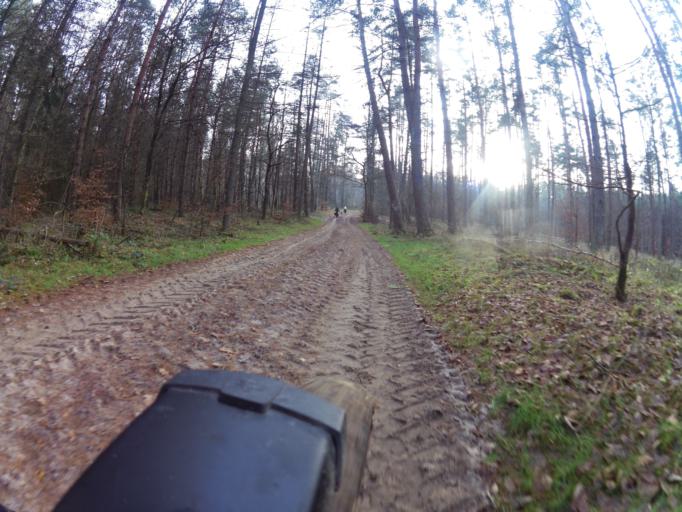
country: PL
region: West Pomeranian Voivodeship
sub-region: Powiat koszalinski
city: Polanow
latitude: 54.1499
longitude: 16.7302
